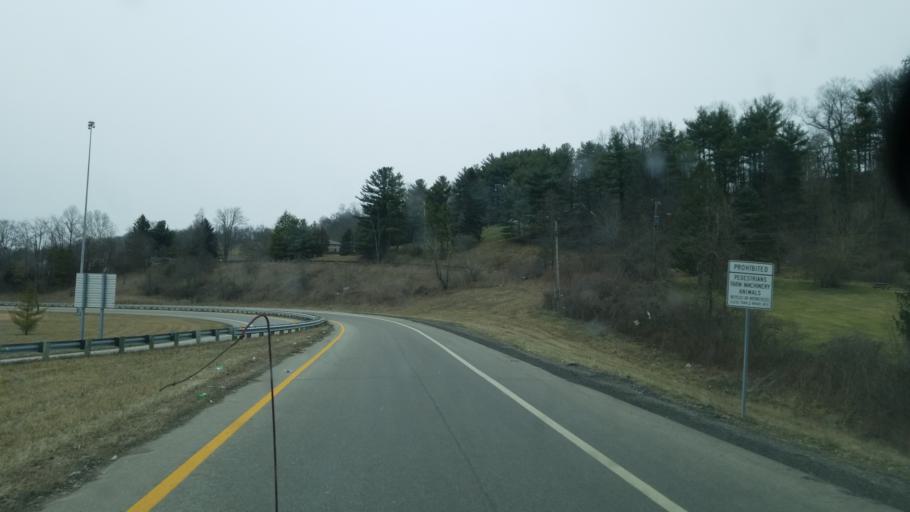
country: US
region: Ohio
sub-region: Guernsey County
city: Cambridge
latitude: 40.0279
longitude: -81.5592
